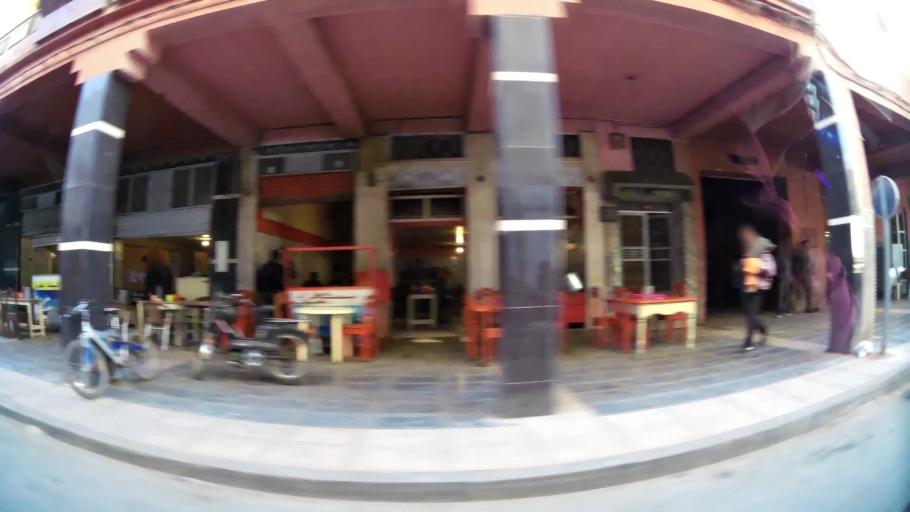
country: MA
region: Oriental
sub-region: Berkane-Taourirt
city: Berkane
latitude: 34.9229
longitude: -2.3357
